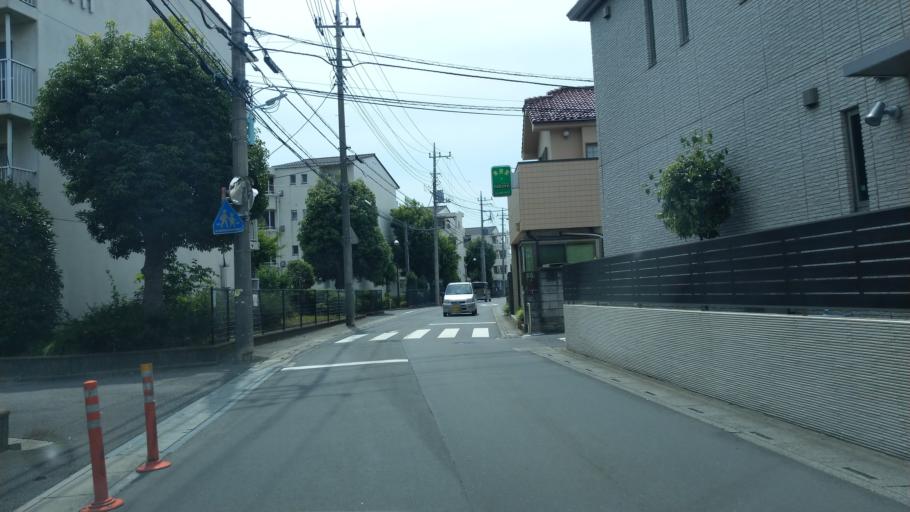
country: JP
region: Saitama
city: Saitama
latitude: 35.9245
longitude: 139.6709
